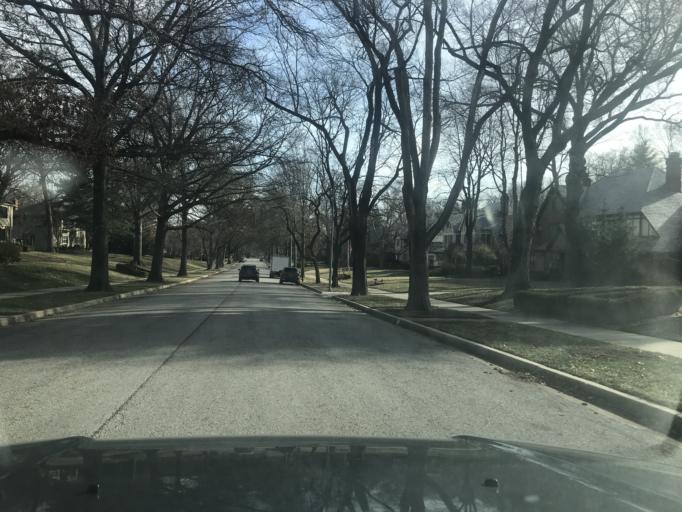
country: US
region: Kansas
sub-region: Johnson County
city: Mission Hills
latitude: 39.0255
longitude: -94.5970
